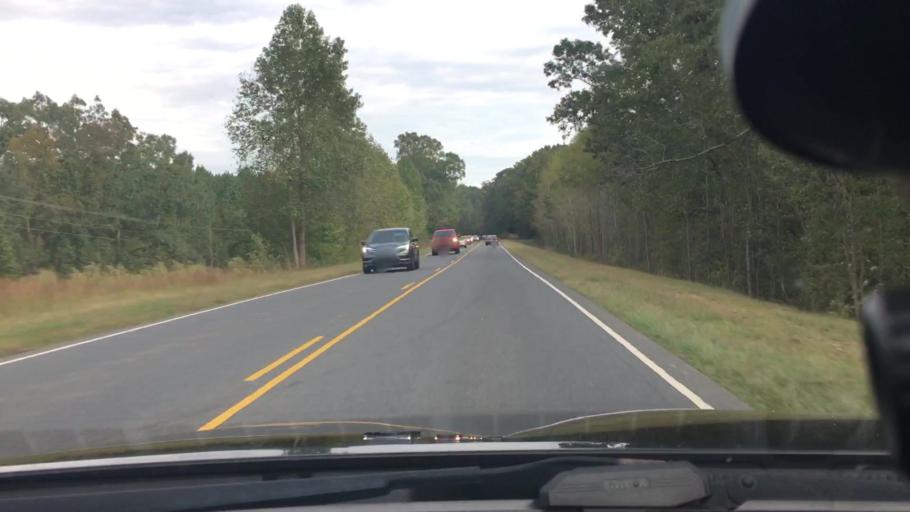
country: US
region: North Carolina
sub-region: Montgomery County
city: Mount Gilead
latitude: 35.3051
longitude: -80.0347
